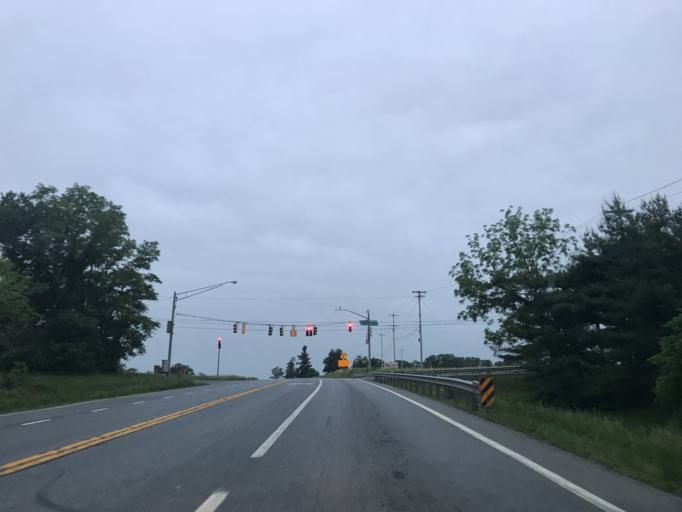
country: US
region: Maryland
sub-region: Frederick County
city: Linganore
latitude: 39.4369
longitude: -77.2534
